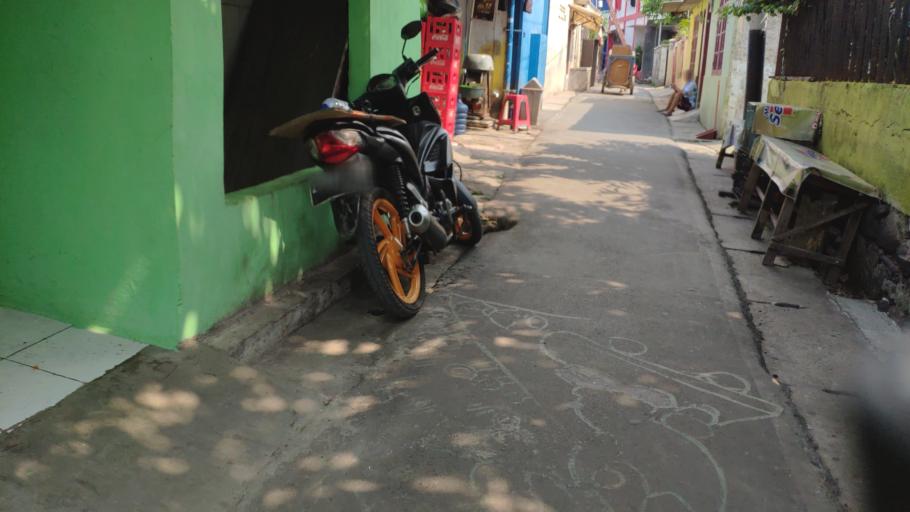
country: ID
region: Jakarta Raya
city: Jakarta
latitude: -6.3024
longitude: 106.8276
